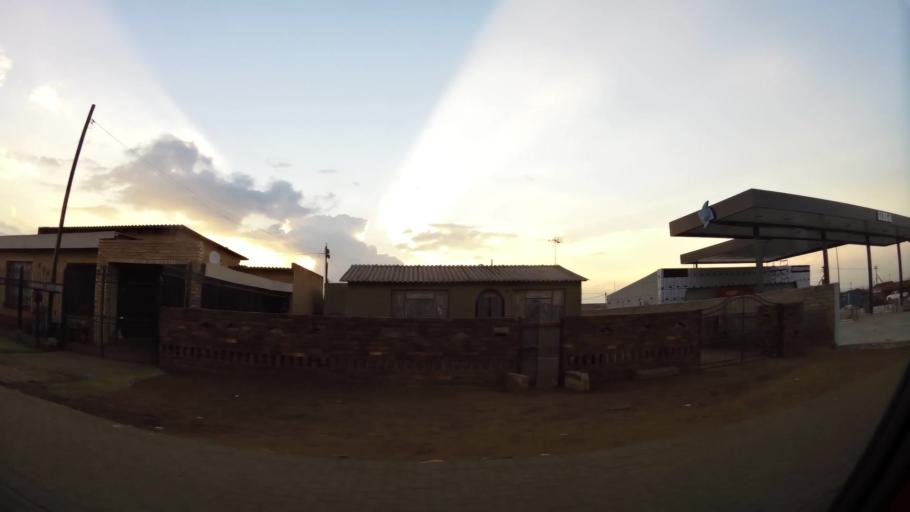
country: ZA
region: Gauteng
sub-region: City of Johannesburg Metropolitan Municipality
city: Orange Farm
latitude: -26.5659
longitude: 27.8496
